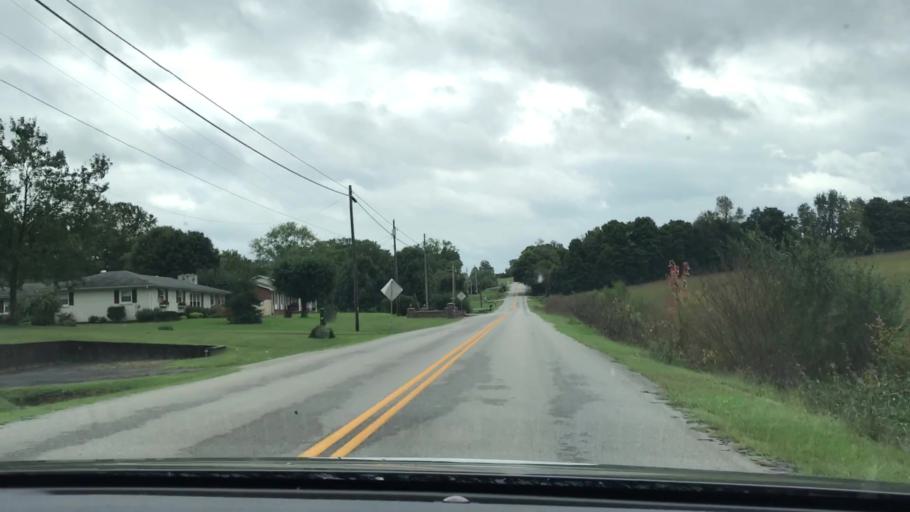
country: US
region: Kentucky
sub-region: Barren County
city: Glasgow
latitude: 36.9616
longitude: -85.8658
